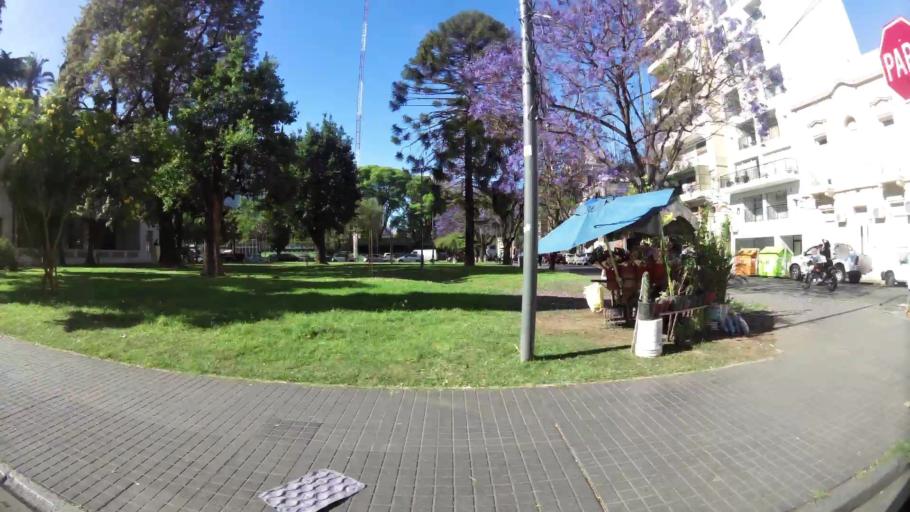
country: AR
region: Santa Fe
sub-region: Departamento de Rosario
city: Rosario
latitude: -32.9452
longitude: -60.6522
